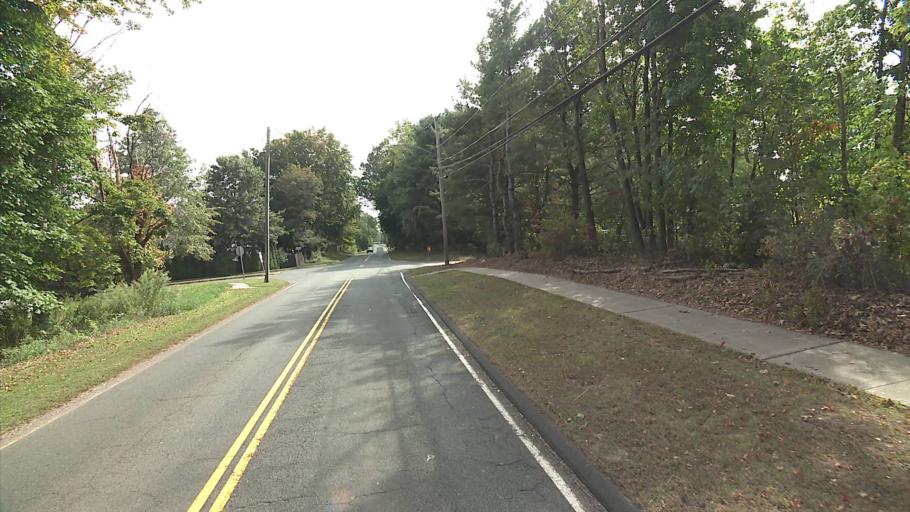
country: US
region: Connecticut
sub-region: Hartford County
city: Newington
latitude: 41.6745
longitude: -72.7194
